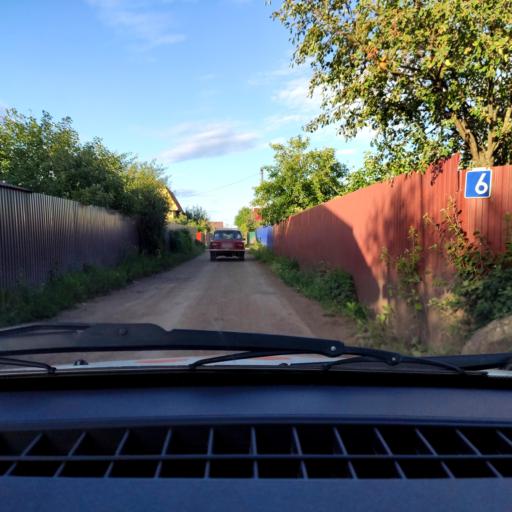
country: RU
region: Bashkortostan
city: Mikhaylovka
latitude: 54.9258
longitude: 55.7496
